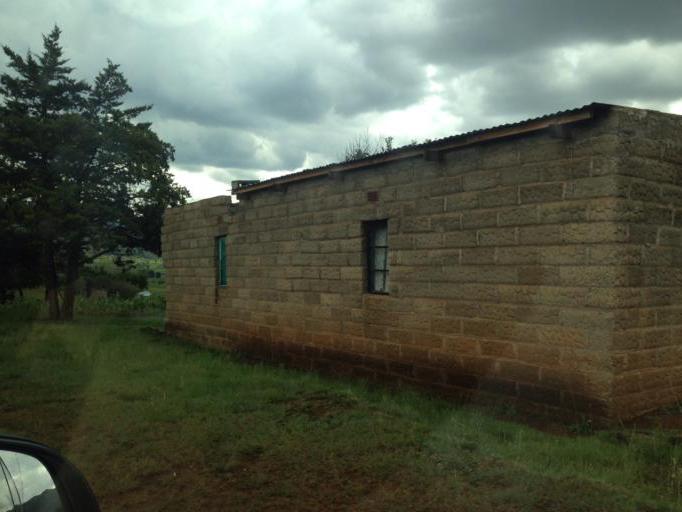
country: LS
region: Maseru
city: Nako
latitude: -29.6239
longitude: 27.7623
